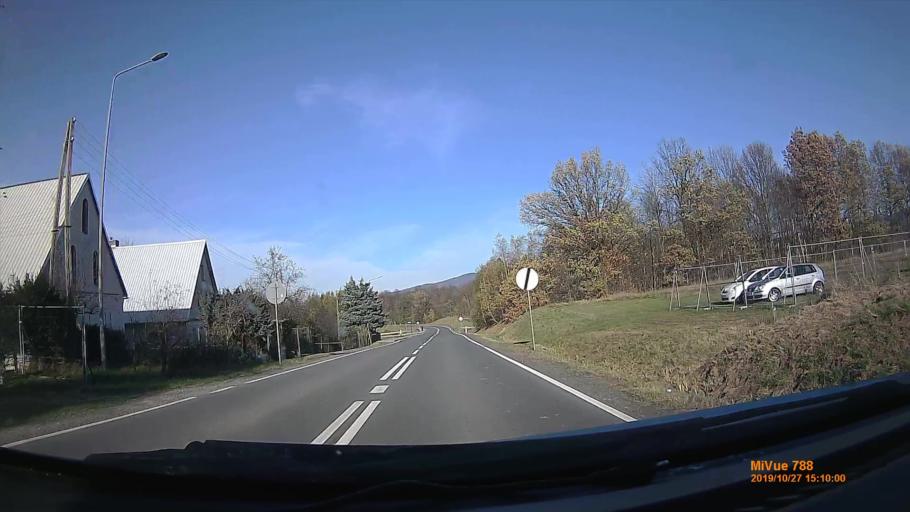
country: PL
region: Lower Silesian Voivodeship
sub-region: Powiat klodzki
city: Miedzylesie
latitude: 50.1844
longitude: 16.6695
